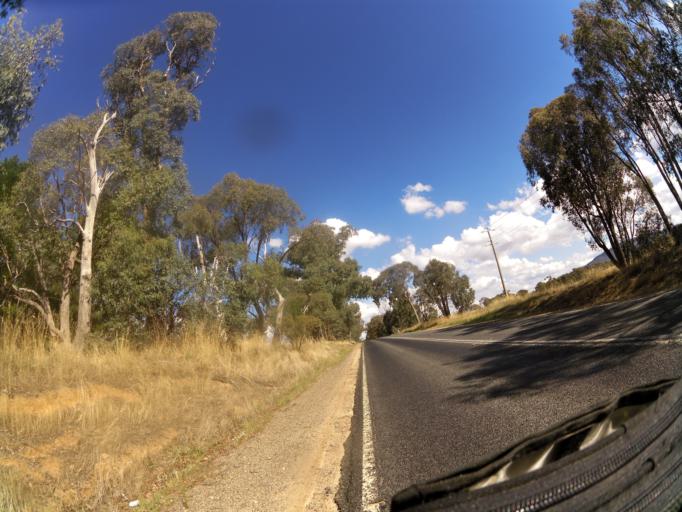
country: AU
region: Victoria
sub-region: Mansfield
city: Mansfield
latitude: -36.9129
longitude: 146.0004
